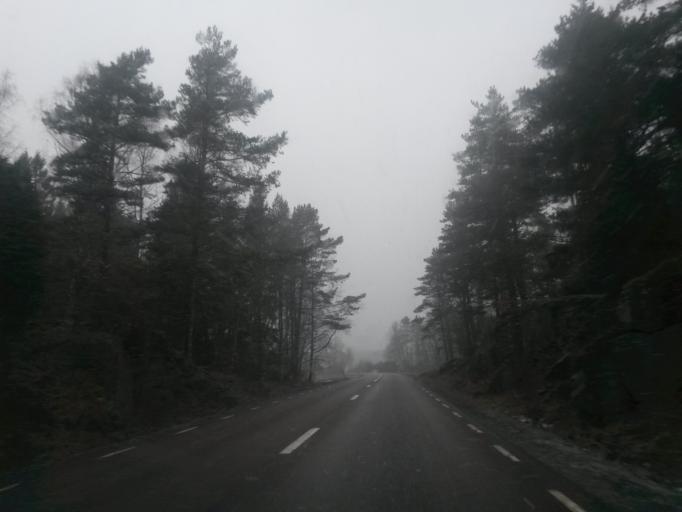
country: SE
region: Vaestra Goetaland
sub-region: Vanersborgs Kommun
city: Vargon
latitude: 58.2251
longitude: 12.4240
